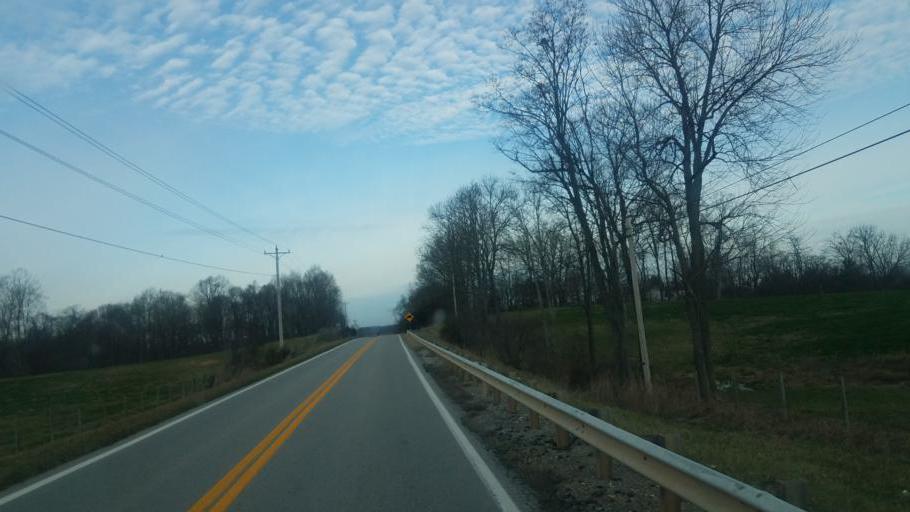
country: US
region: Kentucky
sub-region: Clinton County
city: Albany
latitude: 36.7612
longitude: -85.1602
